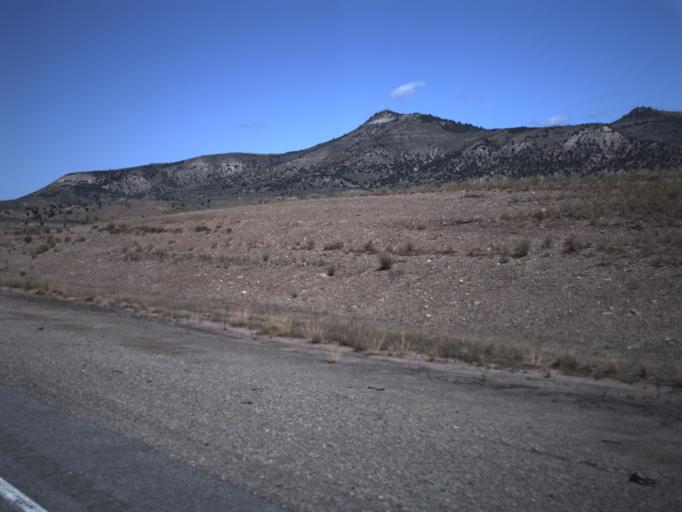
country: US
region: Utah
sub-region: Carbon County
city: Helper
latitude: 39.8369
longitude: -110.9789
